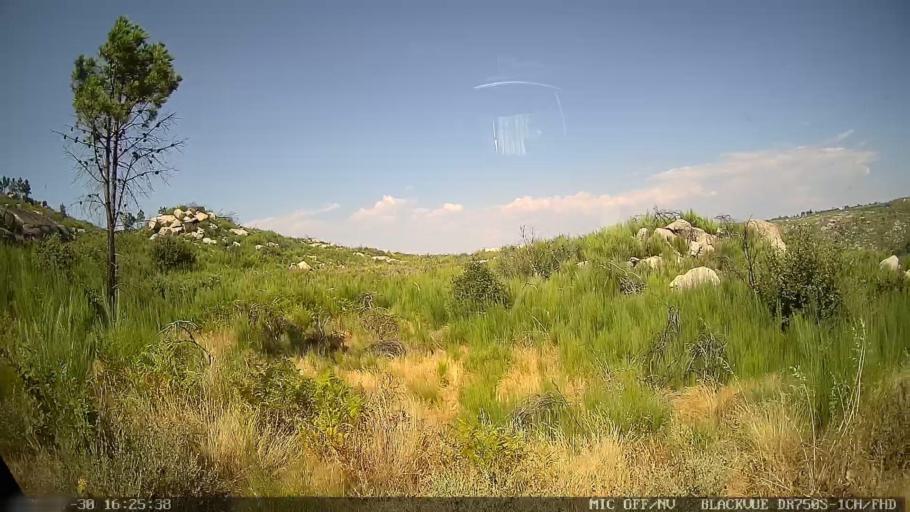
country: PT
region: Vila Real
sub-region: Sabrosa
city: Sabrosa
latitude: 41.3145
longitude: -7.4924
